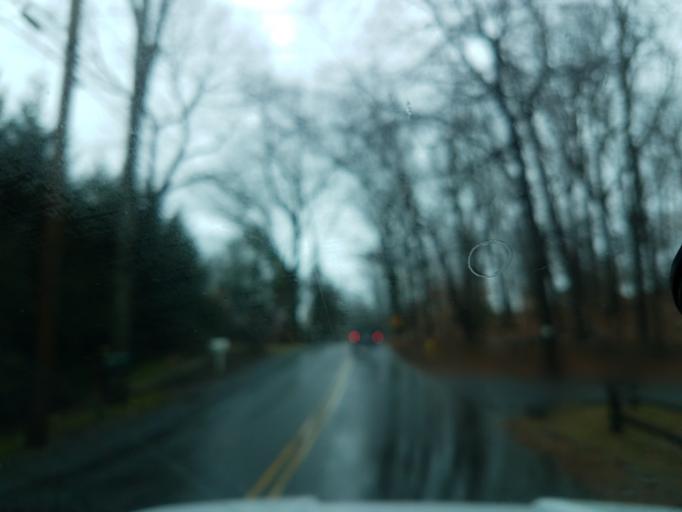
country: US
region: Connecticut
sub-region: Fairfield County
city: Darien
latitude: 41.0962
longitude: -73.4553
